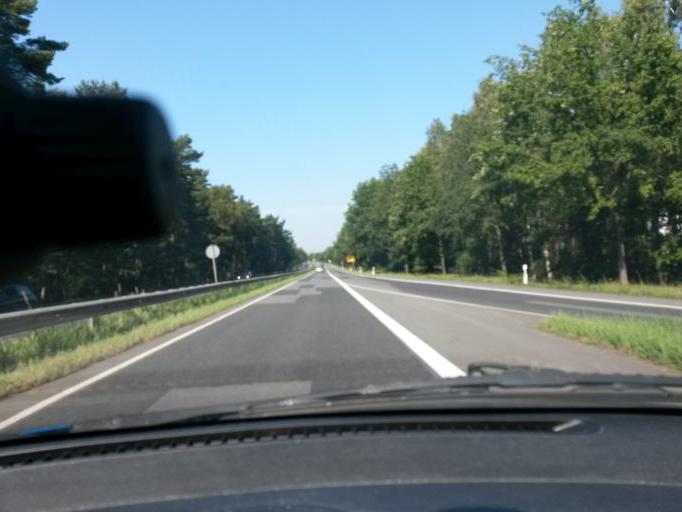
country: DE
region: Lower Saxony
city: Wendisch Evern
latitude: 53.2389
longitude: 10.4708
